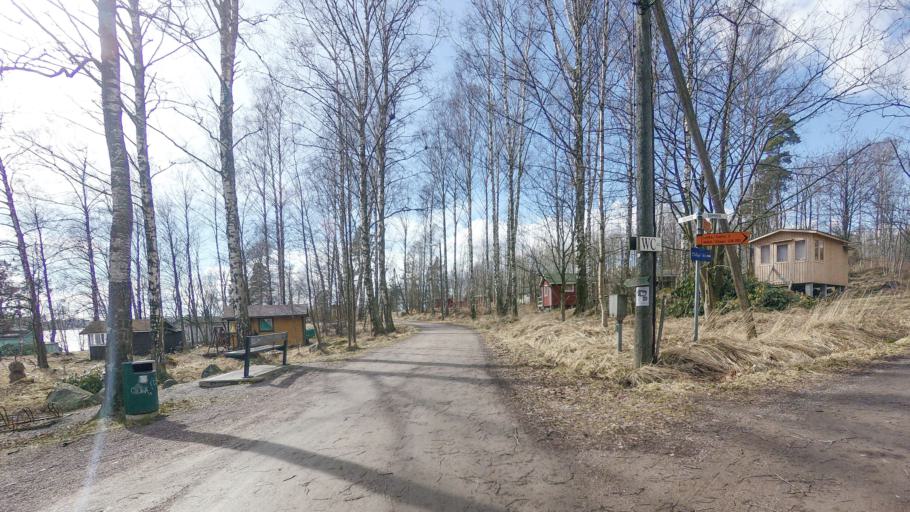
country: FI
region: Uusimaa
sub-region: Helsinki
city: Helsinki
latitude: 60.1955
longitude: 25.0061
